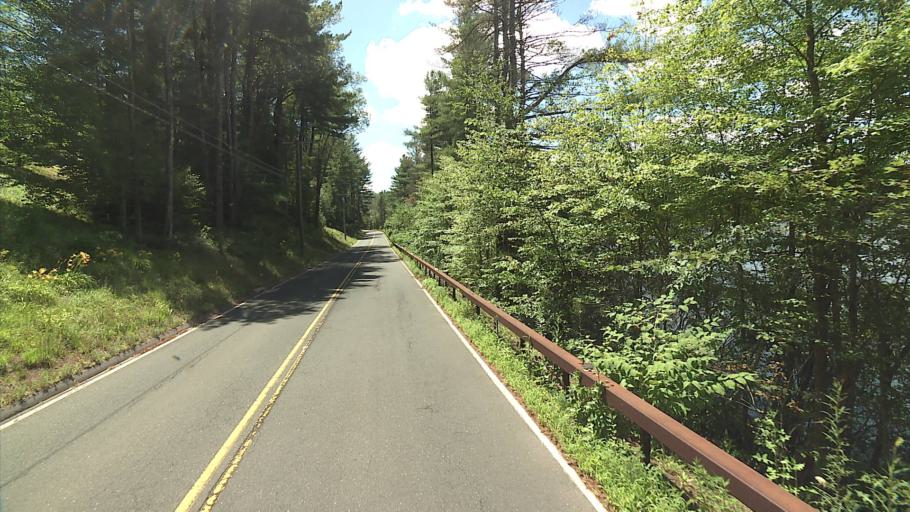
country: US
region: Connecticut
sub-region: Litchfield County
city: New Hartford Center
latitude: 41.8979
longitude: -72.9574
